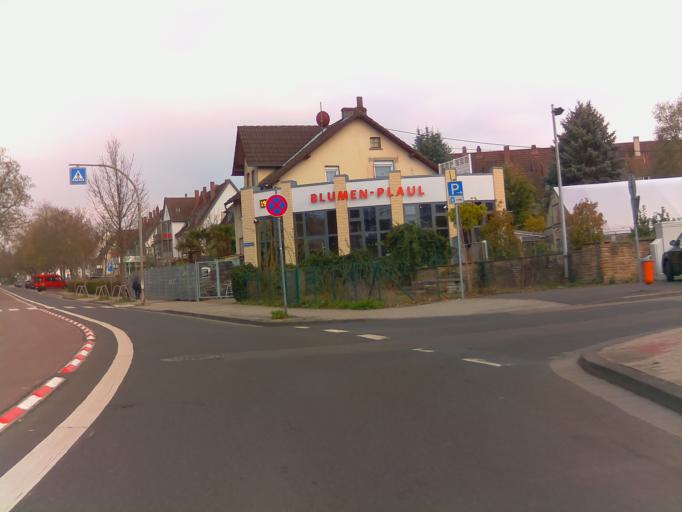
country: DE
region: Rheinland-Pfalz
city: Bad Kreuznach
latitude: 49.8363
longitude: 7.8690
